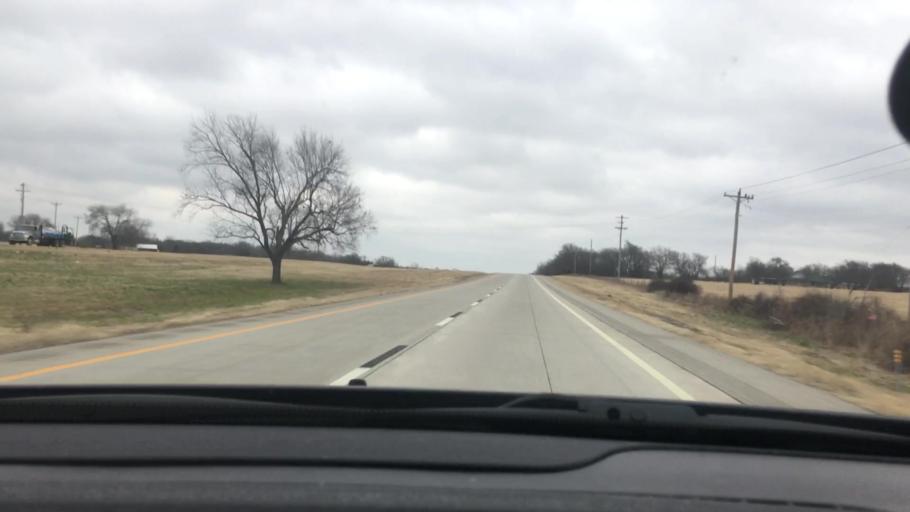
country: US
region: Oklahoma
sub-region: Bryan County
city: Durant
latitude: 34.1754
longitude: -96.2502
